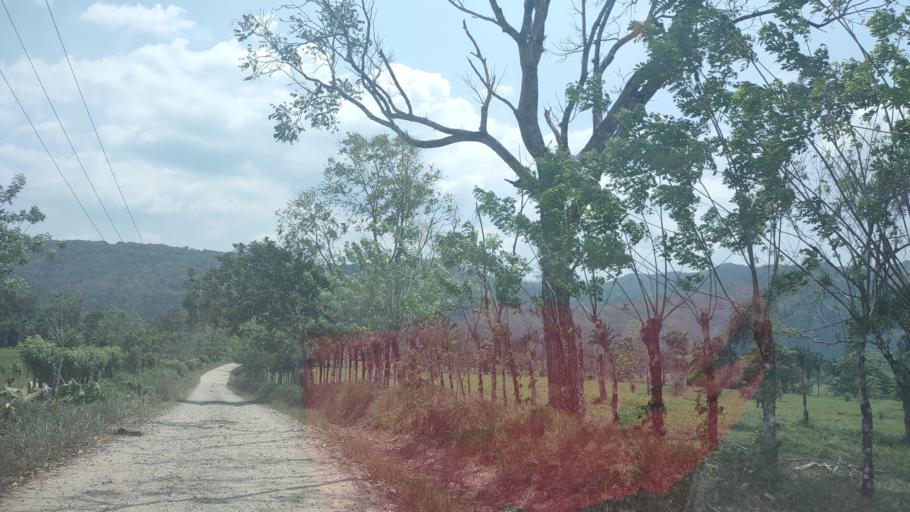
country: MX
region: Chiapas
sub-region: Tecpatan
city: Raudales Malpaso
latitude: 17.2776
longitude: -93.8703
